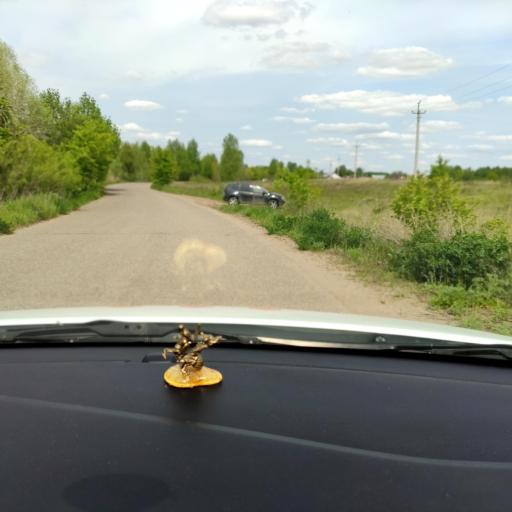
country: RU
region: Tatarstan
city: Verkhniy Uslon
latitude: 55.6967
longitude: 49.0582
